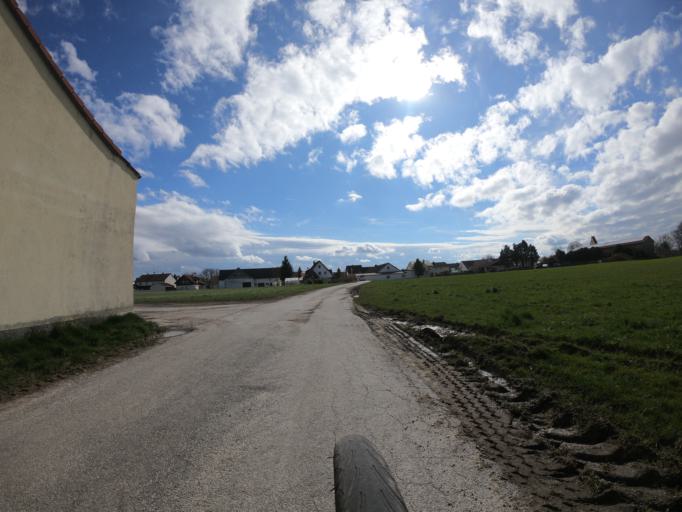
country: DE
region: Bavaria
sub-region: Upper Bavaria
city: Landsberied
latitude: 48.1807
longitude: 11.1899
